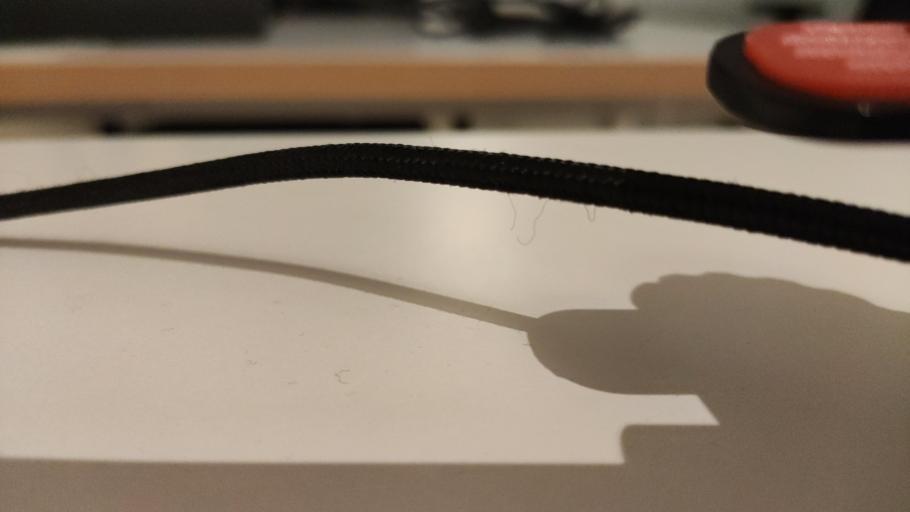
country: RU
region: Moskovskaya
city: Novoye
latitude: 55.6098
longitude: 38.9291
